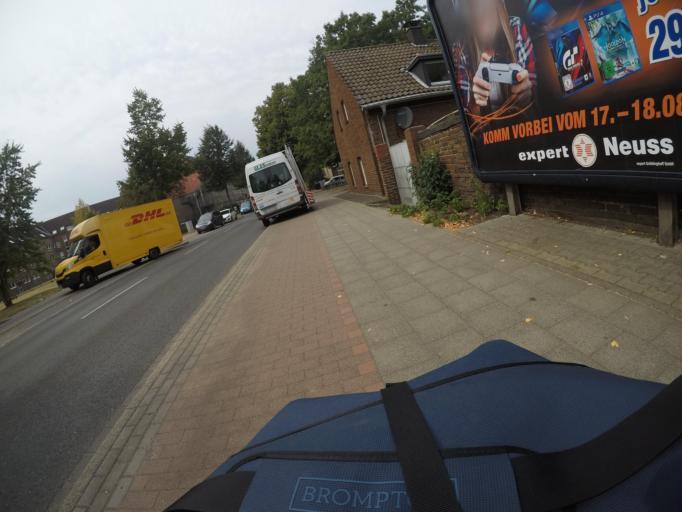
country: DE
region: North Rhine-Westphalia
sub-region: Regierungsbezirk Dusseldorf
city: Dusseldorf
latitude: 51.1766
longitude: 6.7442
